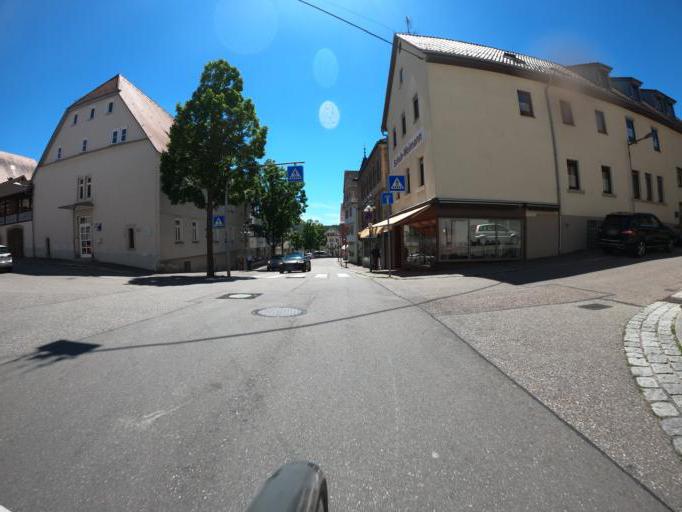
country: DE
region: Baden-Wuerttemberg
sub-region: Regierungsbezirk Stuttgart
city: Vaihingen an der Enz
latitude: 48.9332
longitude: 8.9578
